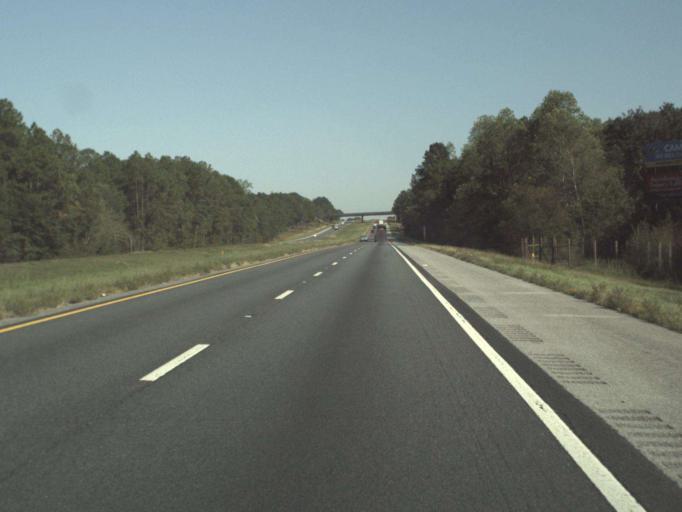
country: US
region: Florida
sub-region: Washington County
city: Chipley
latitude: 30.7529
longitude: -85.5930
